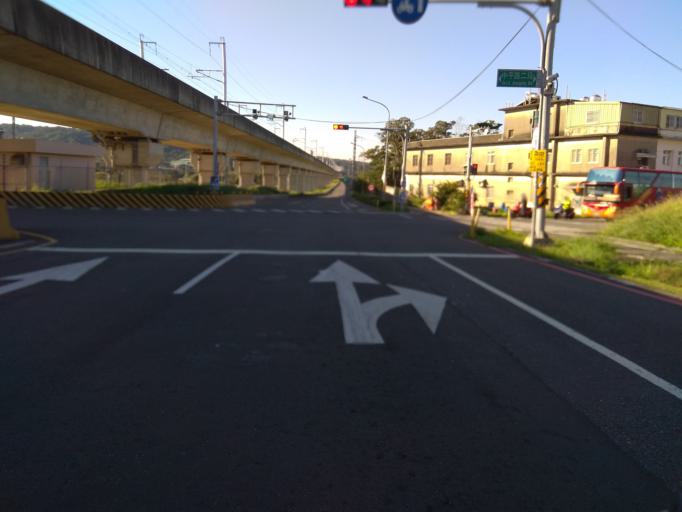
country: TW
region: Taiwan
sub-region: Hsinchu
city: Zhubei
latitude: 24.8913
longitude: 121.0753
